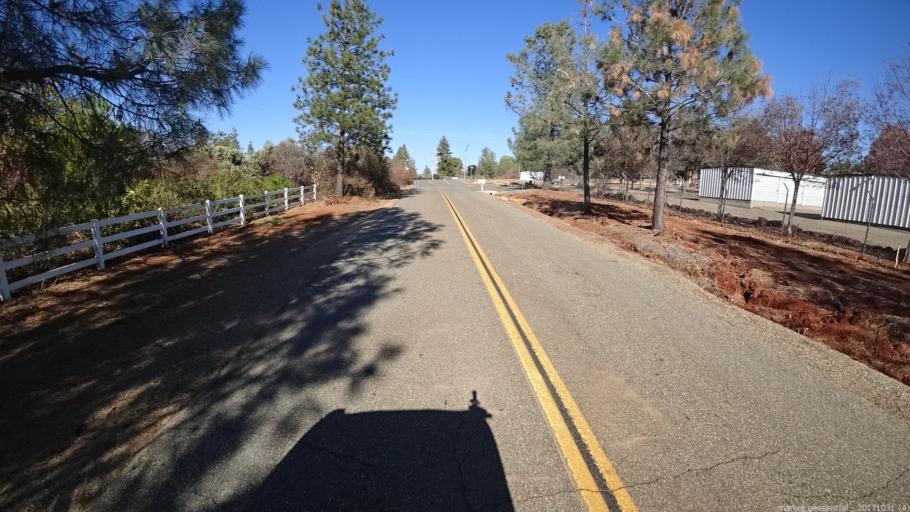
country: US
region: California
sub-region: Shasta County
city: Shingletown
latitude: 40.5007
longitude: -121.9947
